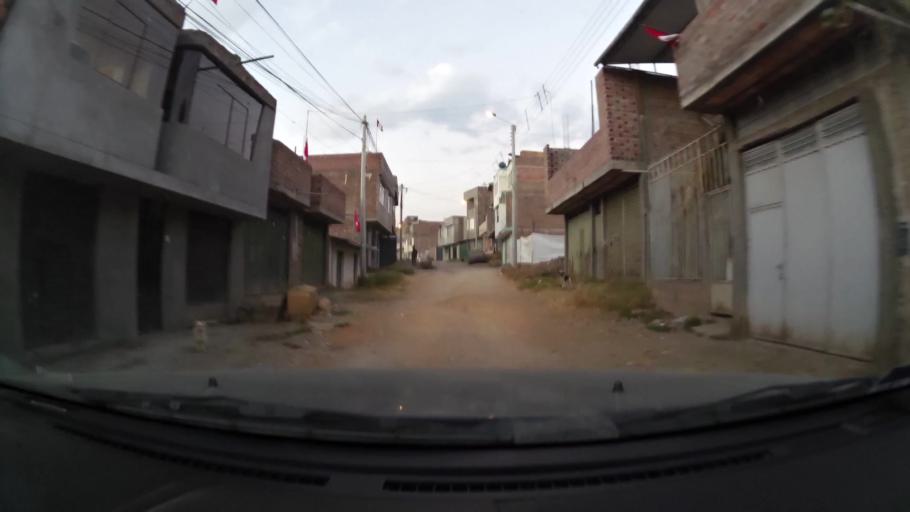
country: PE
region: Junin
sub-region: Provincia de Huancayo
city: El Tambo
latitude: -12.0611
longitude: -75.2310
